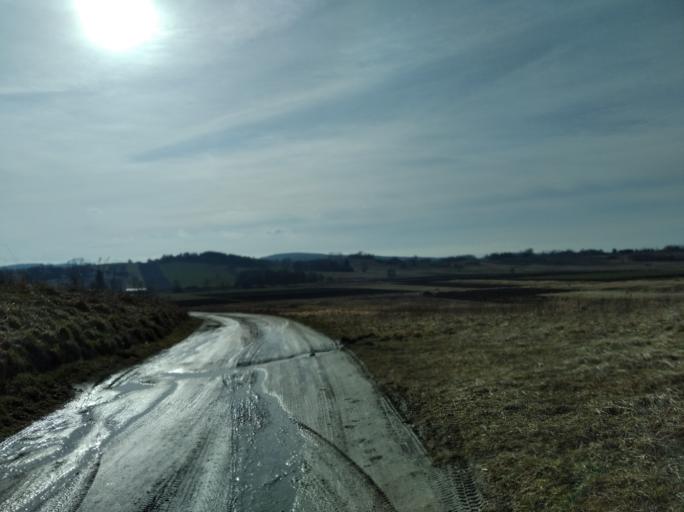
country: PL
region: Subcarpathian Voivodeship
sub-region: Powiat brzozowski
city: Gorki
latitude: 49.6593
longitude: 22.0484
